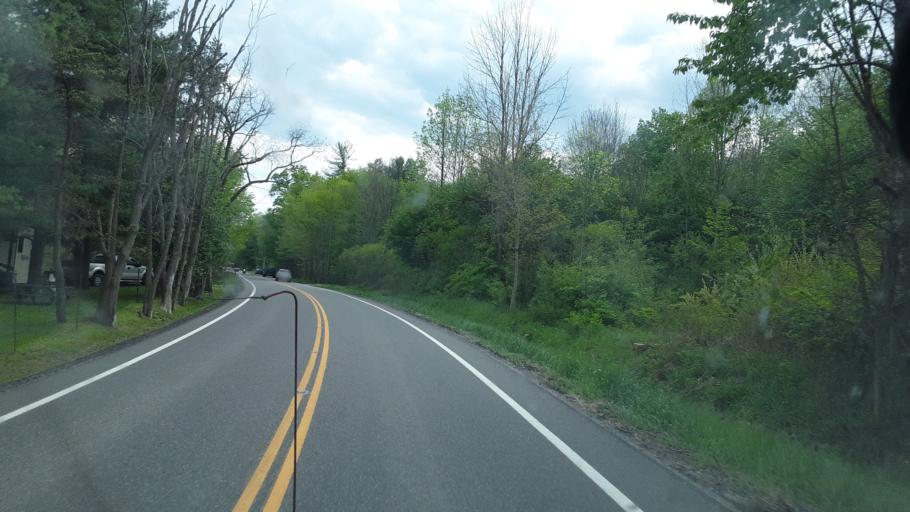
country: US
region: Ohio
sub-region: Portage County
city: Garrettsville
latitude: 41.3462
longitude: -81.0408
